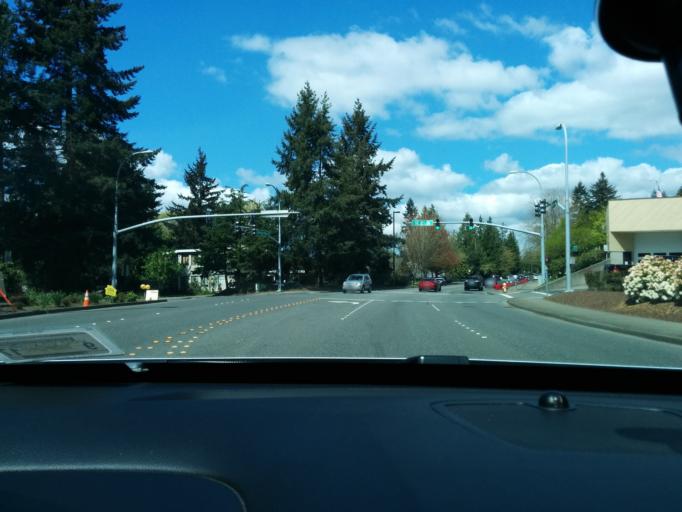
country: US
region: Washington
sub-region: King County
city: Bellevue
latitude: 47.6024
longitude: -122.2010
